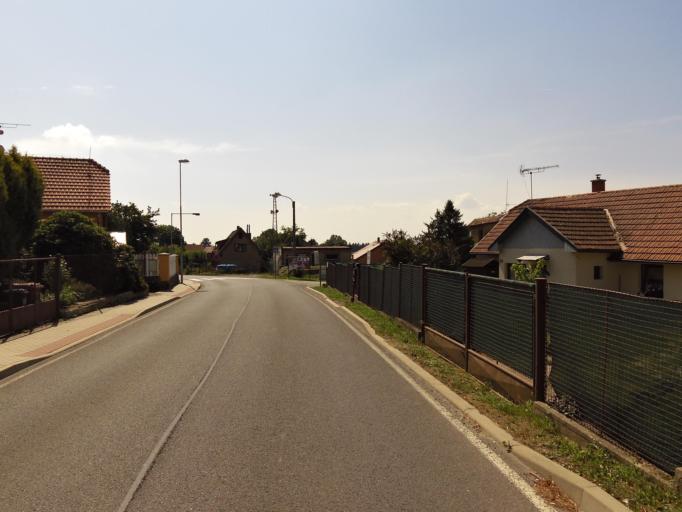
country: CZ
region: Central Bohemia
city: Mukarov
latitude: 49.9550
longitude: 14.7461
